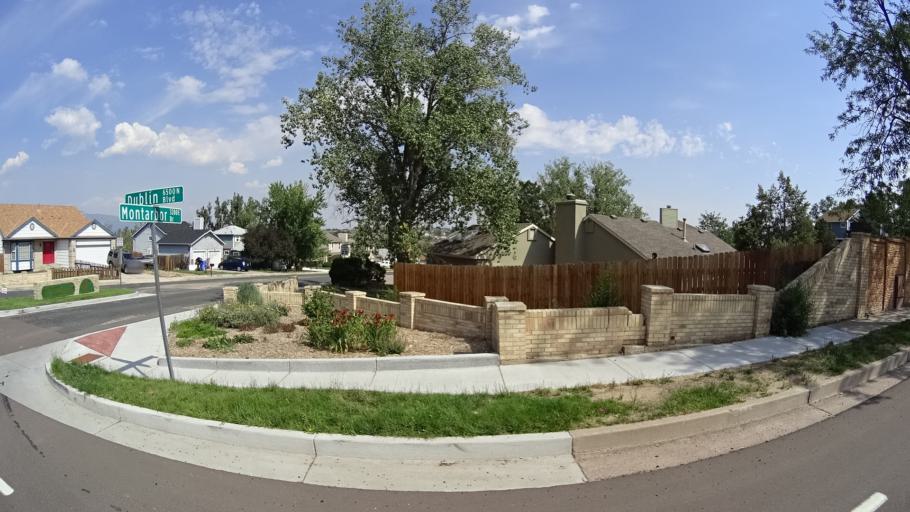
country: US
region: Colorado
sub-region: El Paso County
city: Cimarron Hills
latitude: 38.9253
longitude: -104.7655
